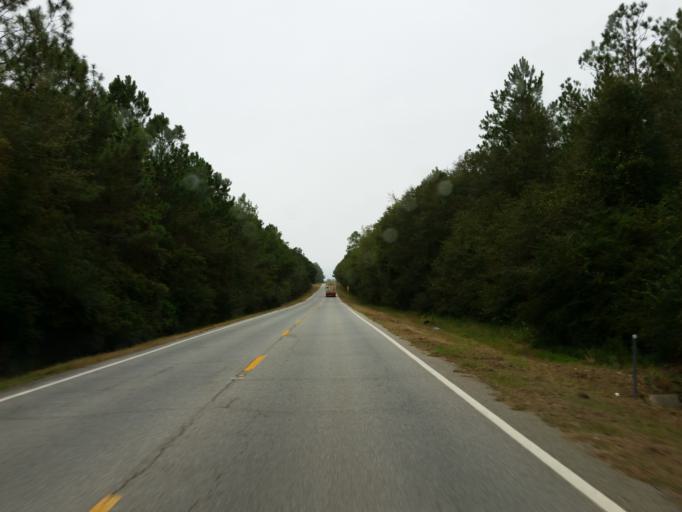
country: US
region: Georgia
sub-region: Berrien County
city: Ray City
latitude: 31.1096
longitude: -83.2928
